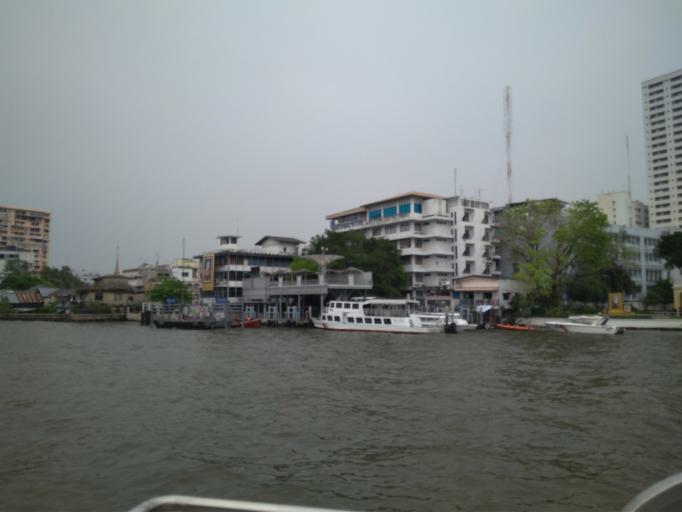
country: TH
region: Bangkok
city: Khlong San
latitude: 13.7316
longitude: 100.5115
